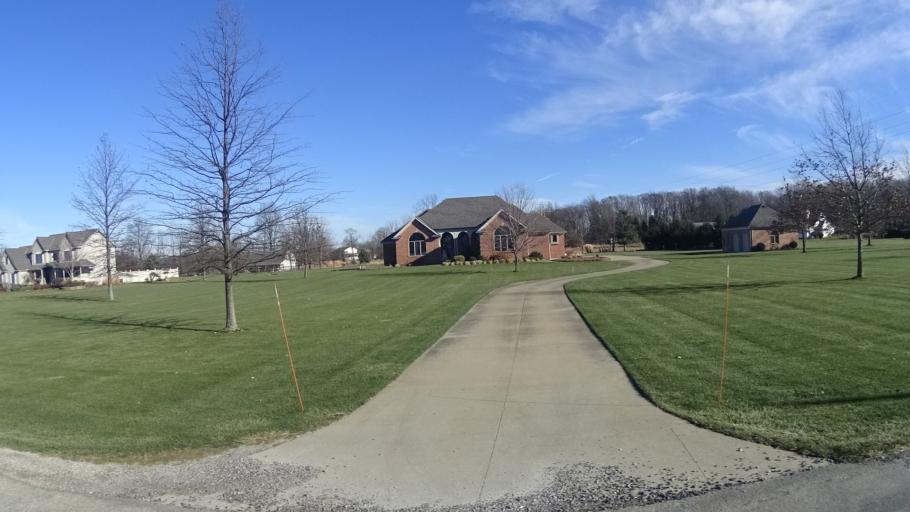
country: US
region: Ohio
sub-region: Lorain County
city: Vermilion-on-the-Lake
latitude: 41.3717
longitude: -82.3293
